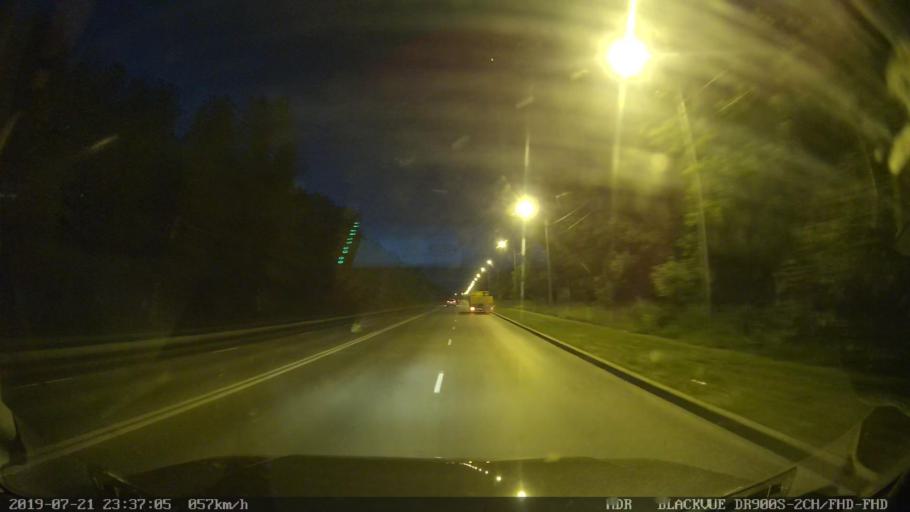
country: RU
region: Perm
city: Kondratovo
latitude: 57.9447
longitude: 56.1723
